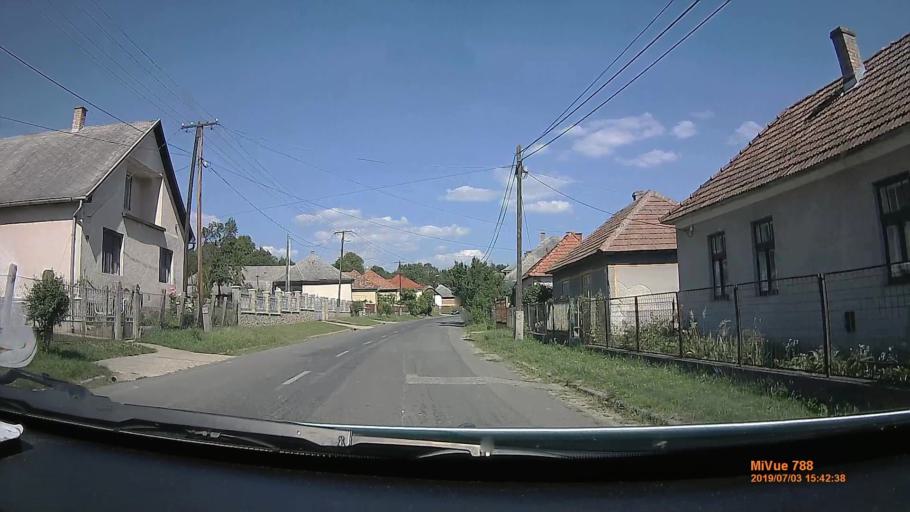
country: HU
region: Heves
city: Szilvasvarad
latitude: 48.1687
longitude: 20.4337
